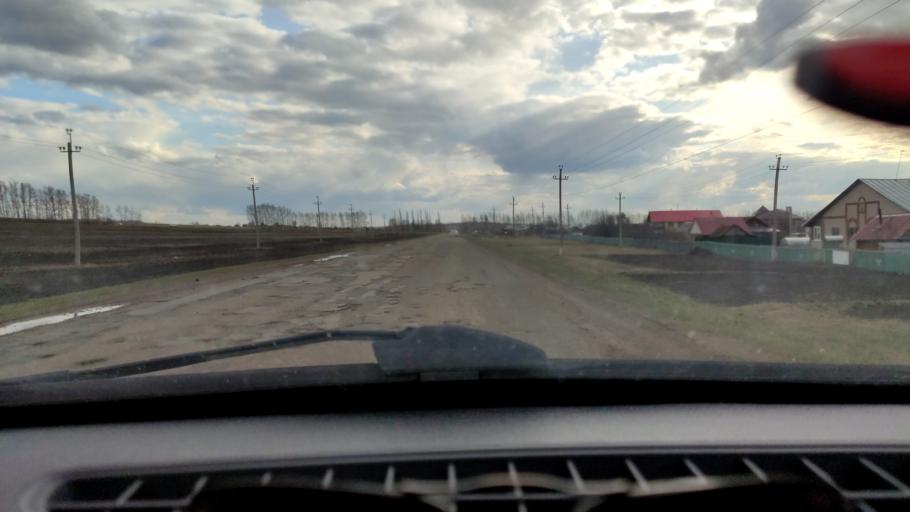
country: RU
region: Bashkortostan
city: Karmaskaly
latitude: 54.3939
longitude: 56.2424
